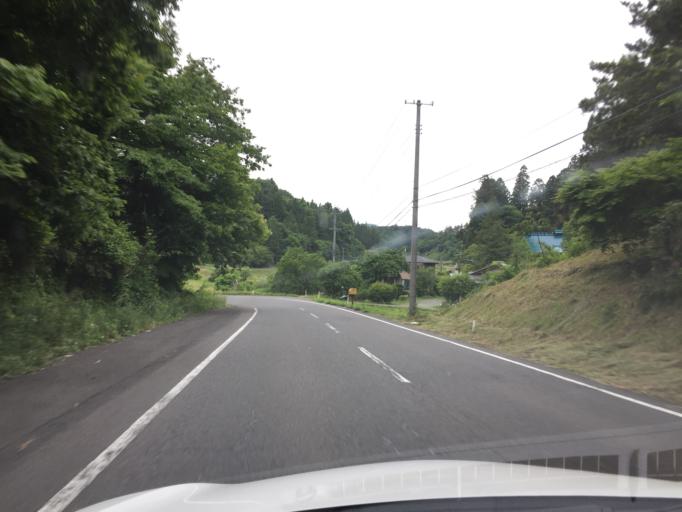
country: JP
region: Fukushima
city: Funehikimachi-funehiki
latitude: 37.3156
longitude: 140.6241
